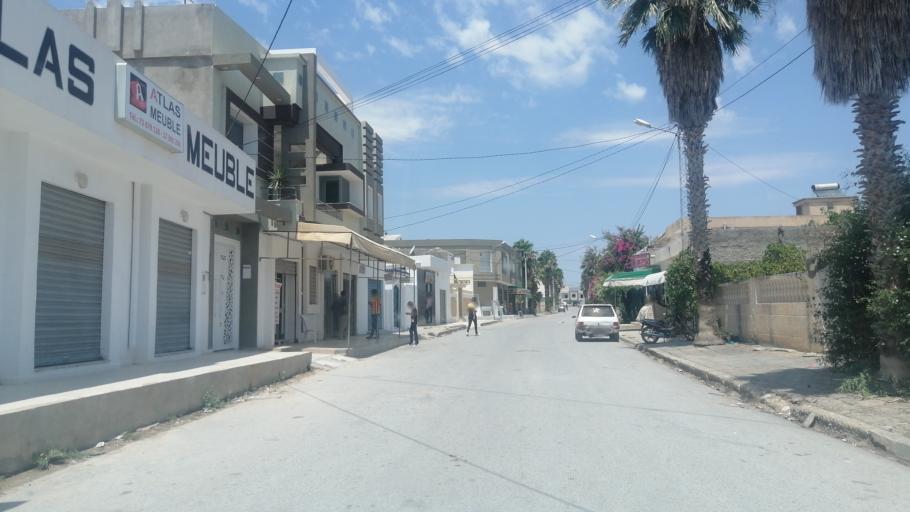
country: TN
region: Al Qayrawan
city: Sbikha
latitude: 36.1205
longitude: 10.0935
